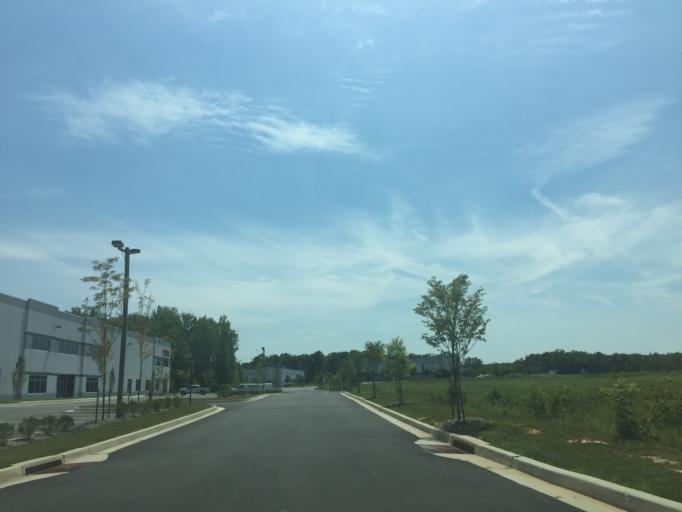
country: US
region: Maryland
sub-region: Baltimore County
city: Bowleys Quarters
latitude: 39.3506
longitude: -76.4086
